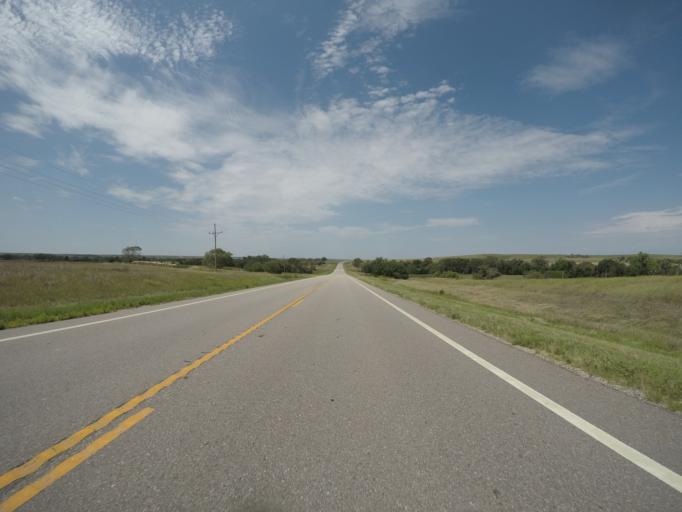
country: US
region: Kansas
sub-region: Rooks County
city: Stockton
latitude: 39.4488
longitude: -99.1487
